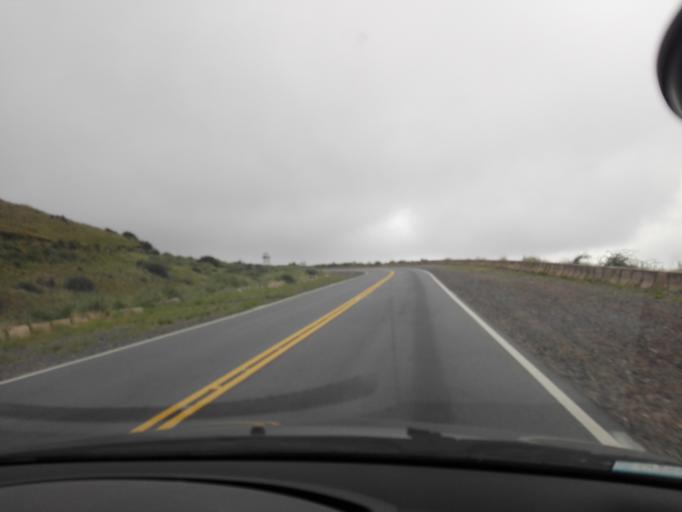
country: AR
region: Cordoba
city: Cuesta Blanca
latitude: -31.6180
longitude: -64.6871
